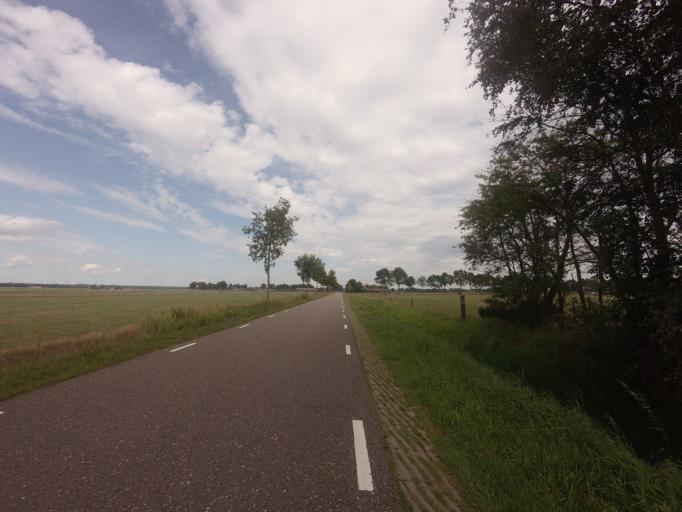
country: NL
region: Overijssel
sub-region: Gemeente Dalfsen
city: Dalfsen
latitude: 52.4658
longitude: 6.3577
